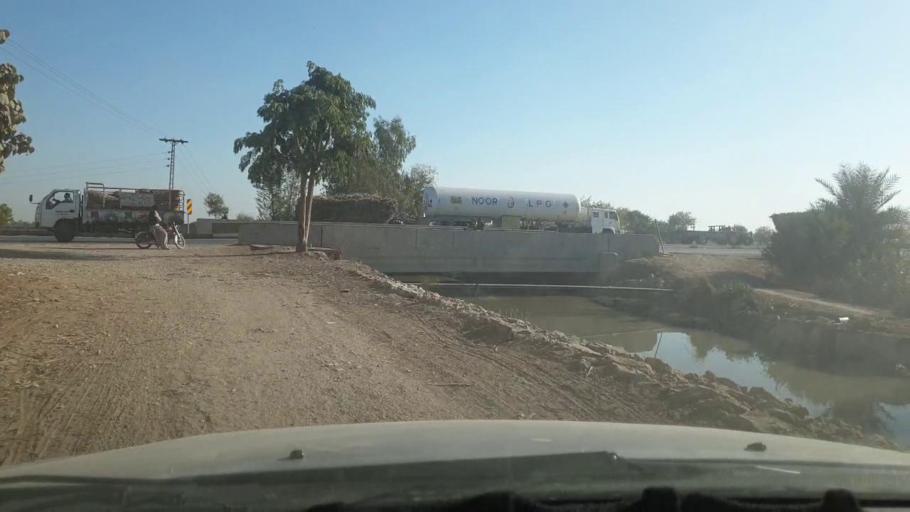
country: PK
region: Sindh
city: Adilpur
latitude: 27.9400
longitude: 69.2212
